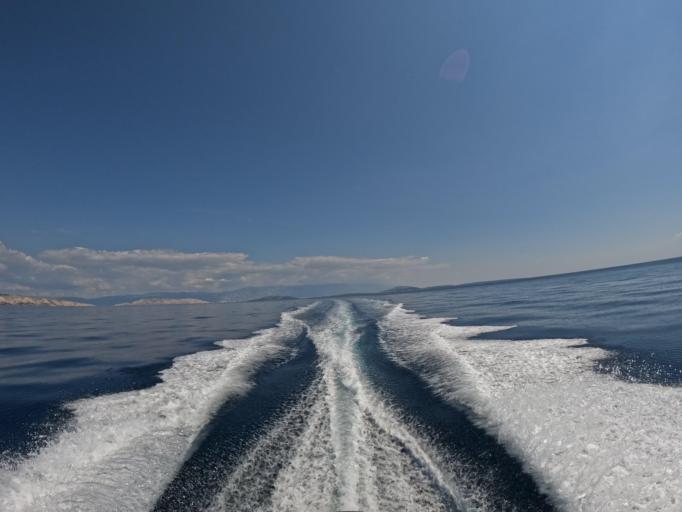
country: HR
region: Primorsko-Goranska
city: Punat
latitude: 44.9131
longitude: 14.5855
